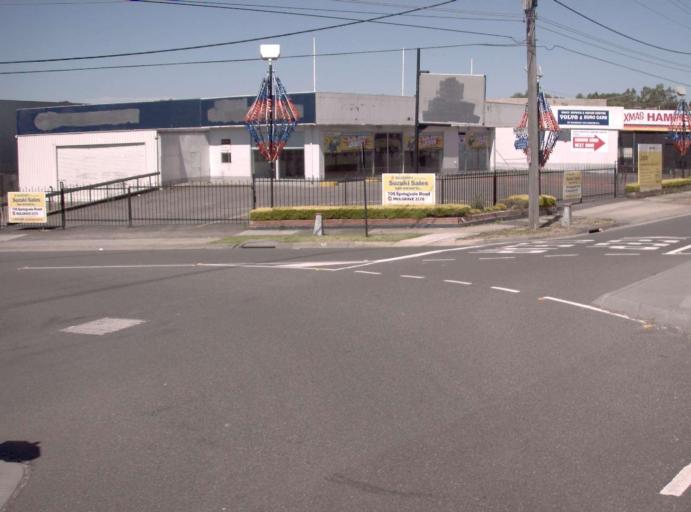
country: AU
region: Victoria
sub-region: Monash
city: Chadstone
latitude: -37.8947
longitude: 145.0956
